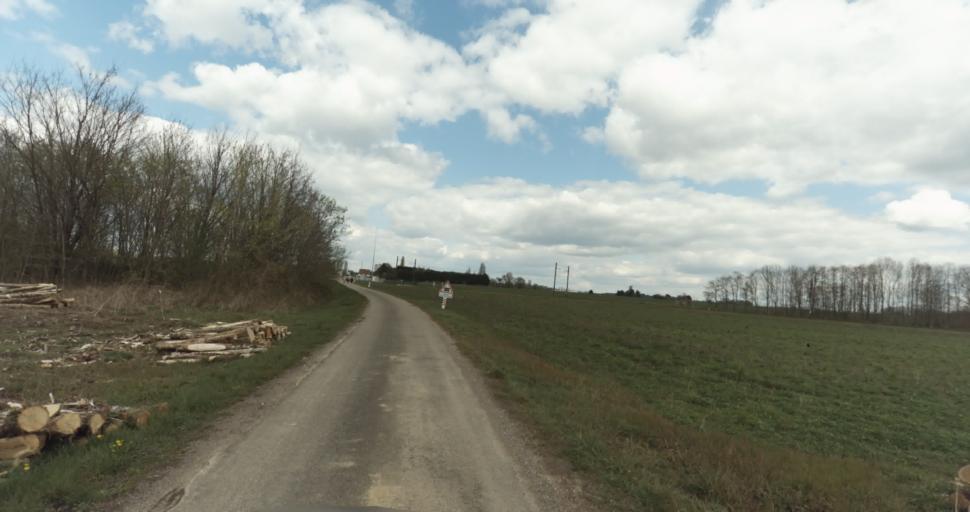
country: FR
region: Bourgogne
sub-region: Departement de la Cote-d'Or
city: Auxonne
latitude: 47.1714
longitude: 5.3946
